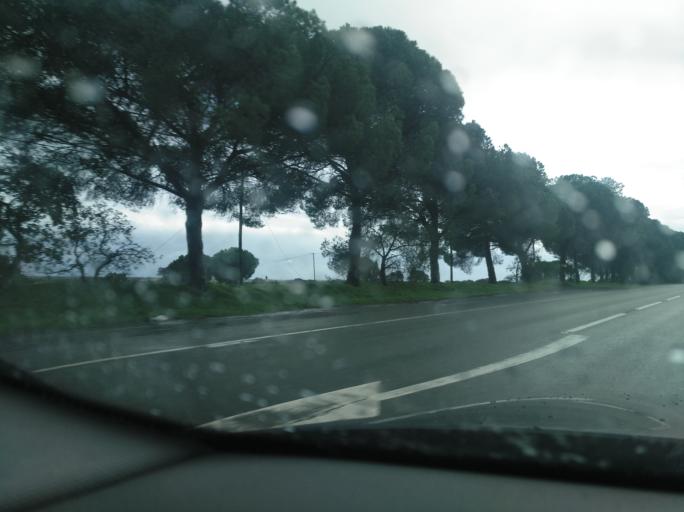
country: PT
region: Setubal
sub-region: Grandola
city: Grandola
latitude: 38.0990
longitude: -8.4184
